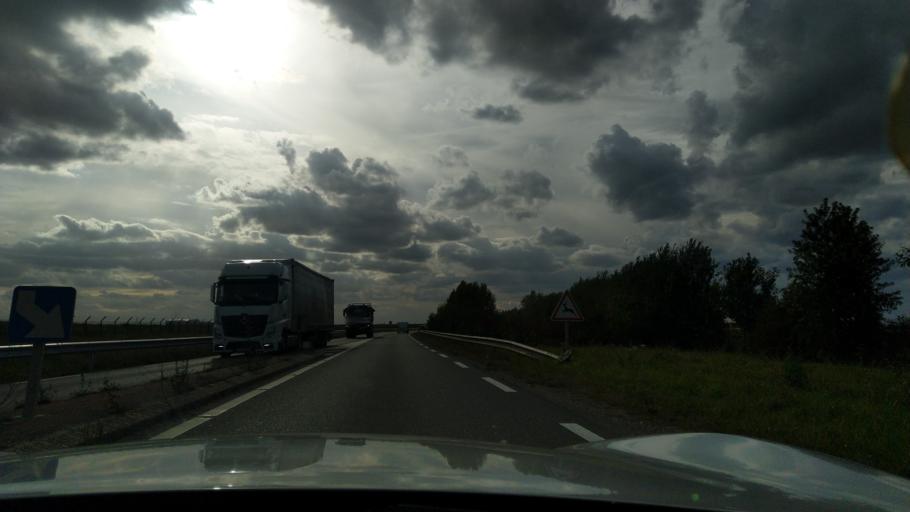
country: FR
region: Ile-de-France
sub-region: Departement du Val-d'Oise
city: Vemars
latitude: 49.0285
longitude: 2.5571
